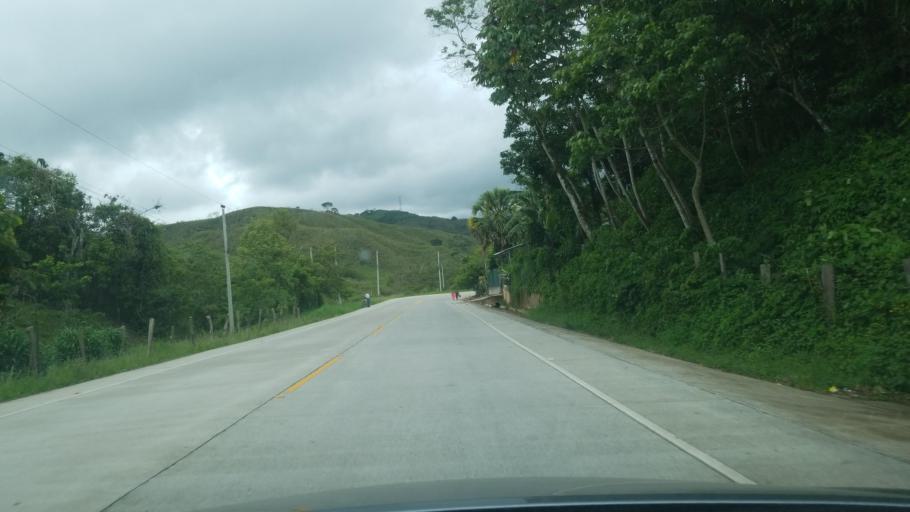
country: HN
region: Copan
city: San Jeronimo
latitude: 14.9418
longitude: -88.9153
